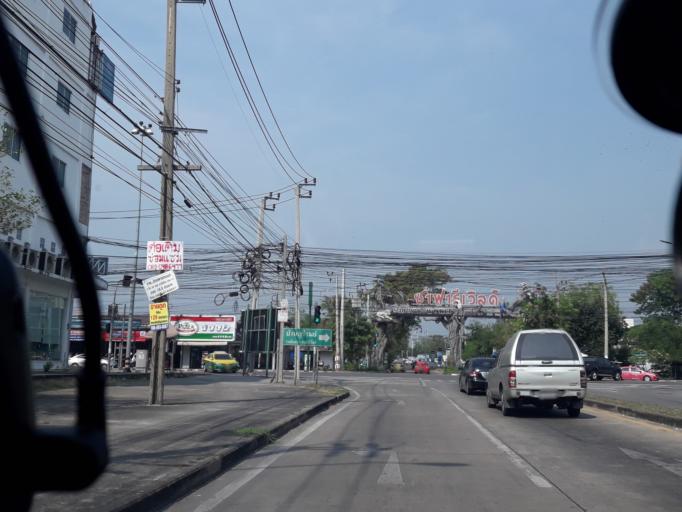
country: TH
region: Bangkok
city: Khlong Sam Wa
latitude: 13.8598
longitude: 100.7071
